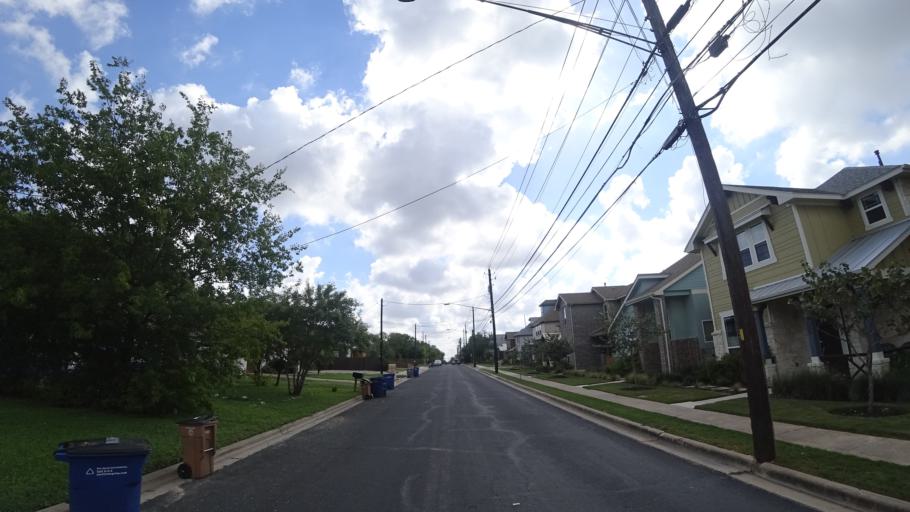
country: US
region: Texas
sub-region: Travis County
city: Austin
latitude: 30.3453
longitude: -97.7178
